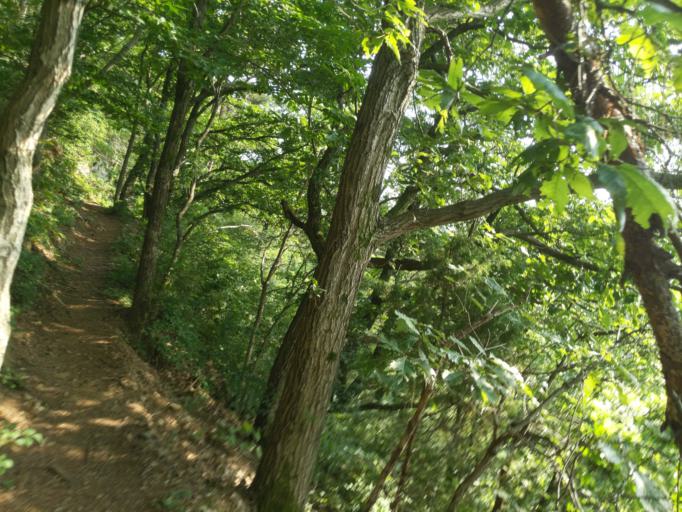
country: KR
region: Daegu
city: Hwawon
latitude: 35.7901
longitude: 128.5406
